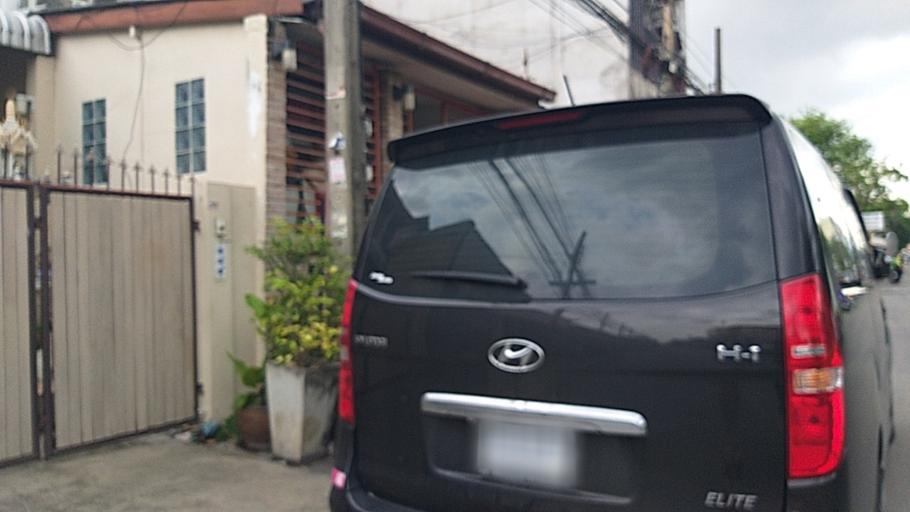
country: TH
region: Bangkok
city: Suan Luang
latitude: 13.7131
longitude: 100.6580
